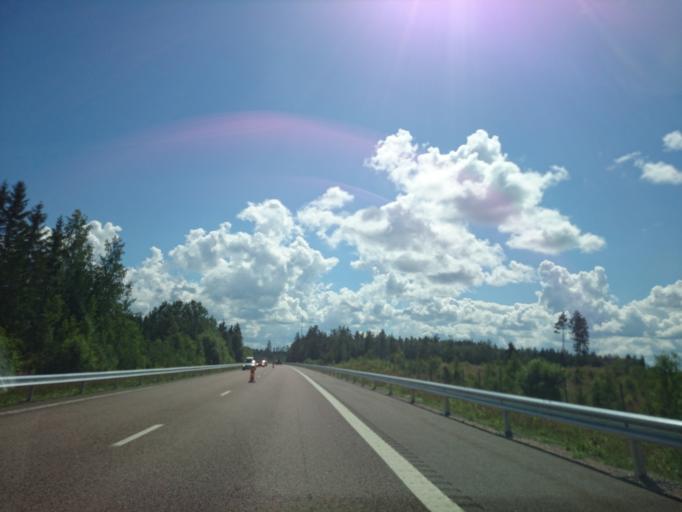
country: SE
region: Uppsala
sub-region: Alvkarleby Kommun
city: Skutskaer
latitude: 60.5219
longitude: 17.2769
